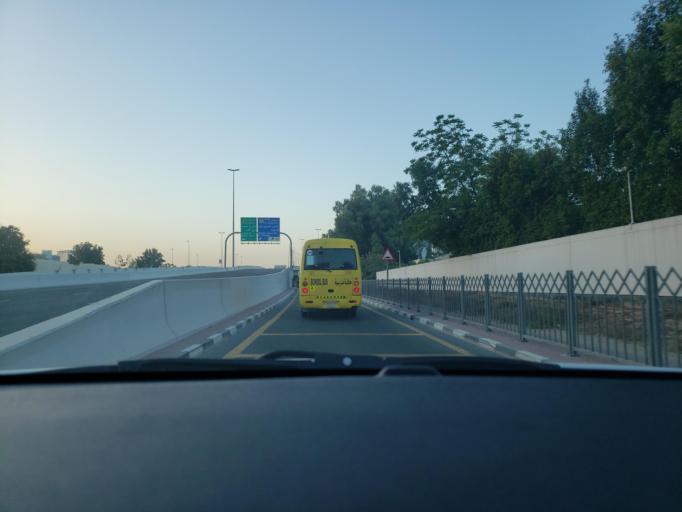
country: AE
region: Dubai
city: Dubai
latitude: 25.1062
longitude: 55.1734
